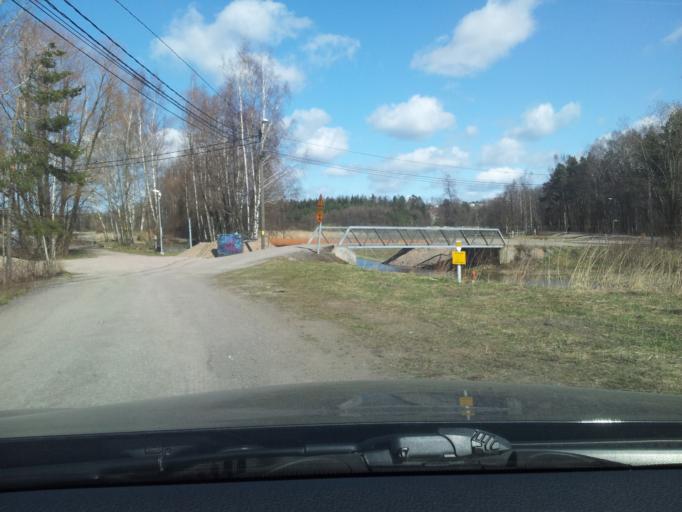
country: FI
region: Uusimaa
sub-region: Helsinki
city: Koukkuniemi
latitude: 60.1497
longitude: 24.7224
